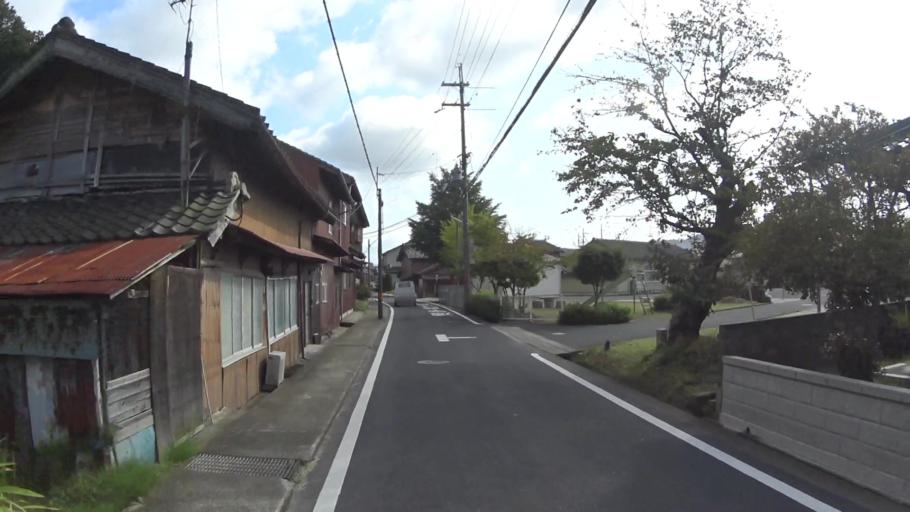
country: JP
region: Kyoto
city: Miyazu
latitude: 35.6151
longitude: 135.0830
